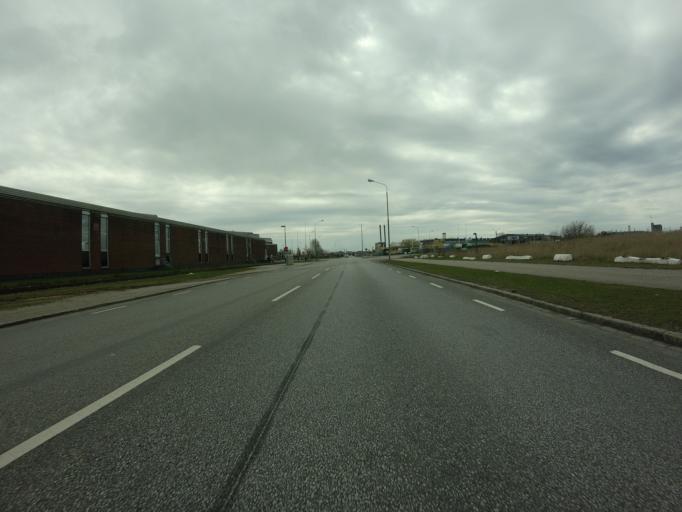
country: SE
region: Skane
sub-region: Burlovs Kommun
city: Arloev
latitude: 55.6247
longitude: 13.0451
